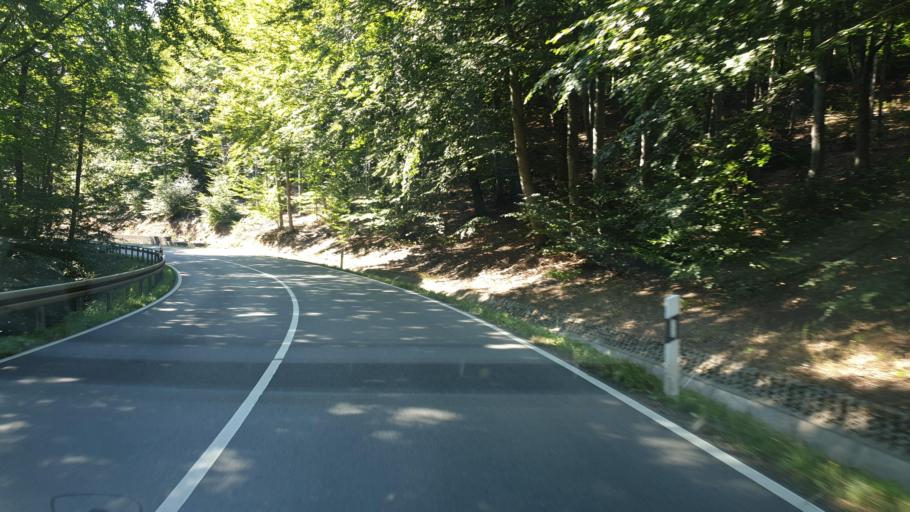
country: DE
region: Saxony
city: Lauter
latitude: 50.5876
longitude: 12.7373
